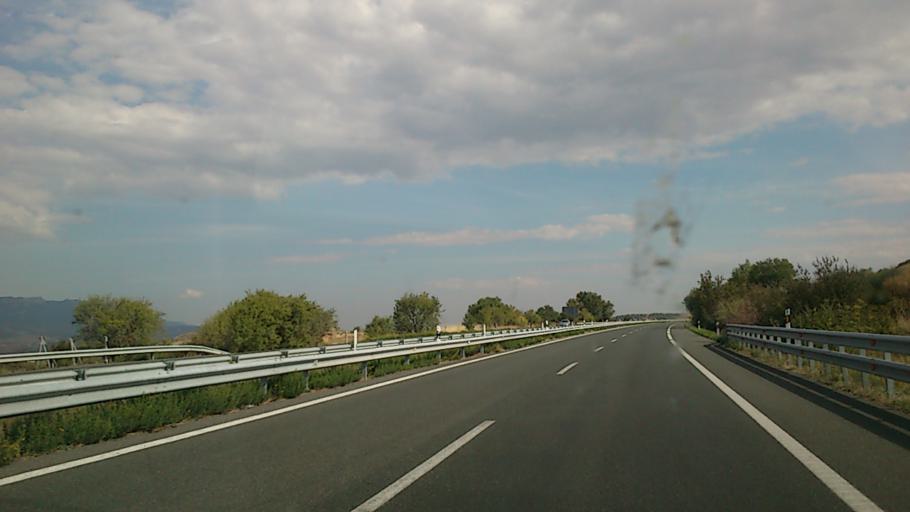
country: ES
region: La Rioja
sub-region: Provincia de La Rioja
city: Ollauri
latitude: 42.5516
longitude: -2.8575
